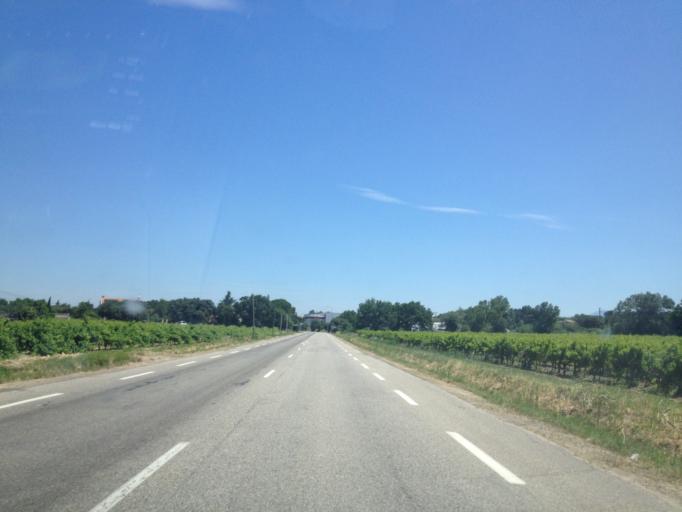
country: FR
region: Provence-Alpes-Cote d'Azur
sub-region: Departement du Vaucluse
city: Bedarrides
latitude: 44.0324
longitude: 4.8860
